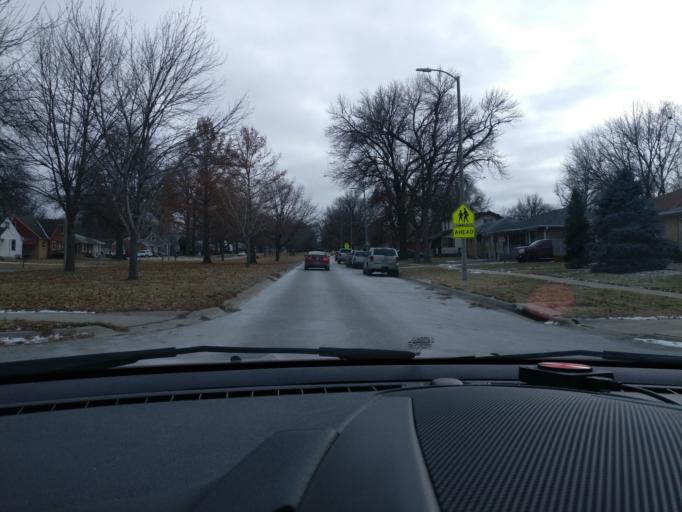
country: US
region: Nebraska
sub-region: Lancaster County
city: Lincoln
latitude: 40.8465
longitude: -96.6402
